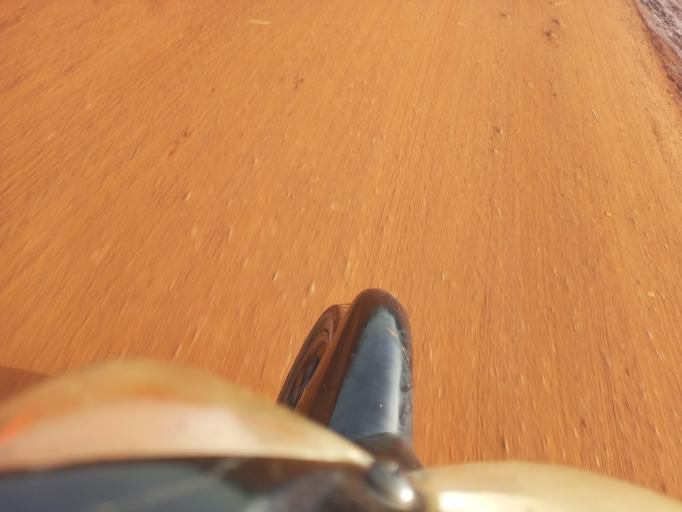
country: ML
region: Bamako
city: Bamako
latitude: 12.5325
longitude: -7.9943
